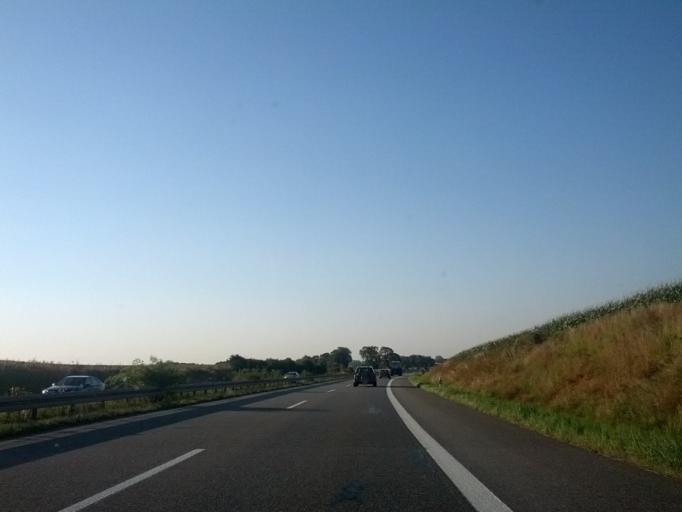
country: DE
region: Mecklenburg-Vorpommern
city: Wendorf
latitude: 54.2778
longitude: 13.0780
